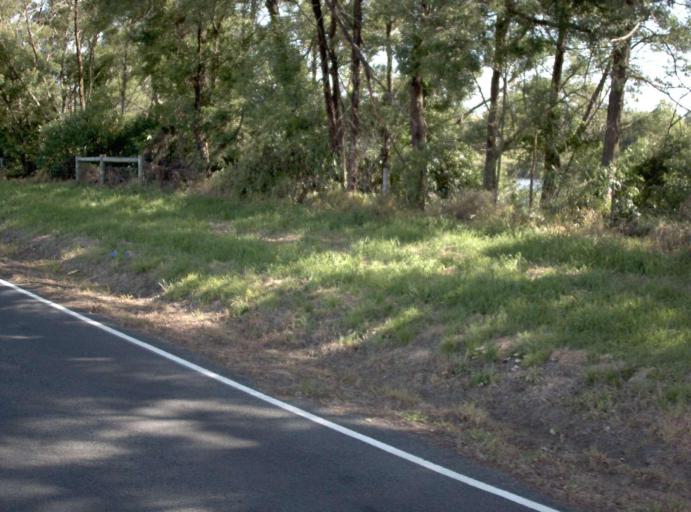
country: AU
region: Victoria
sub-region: East Gippsland
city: Lakes Entrance
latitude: -37.7444
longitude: 148.5148
